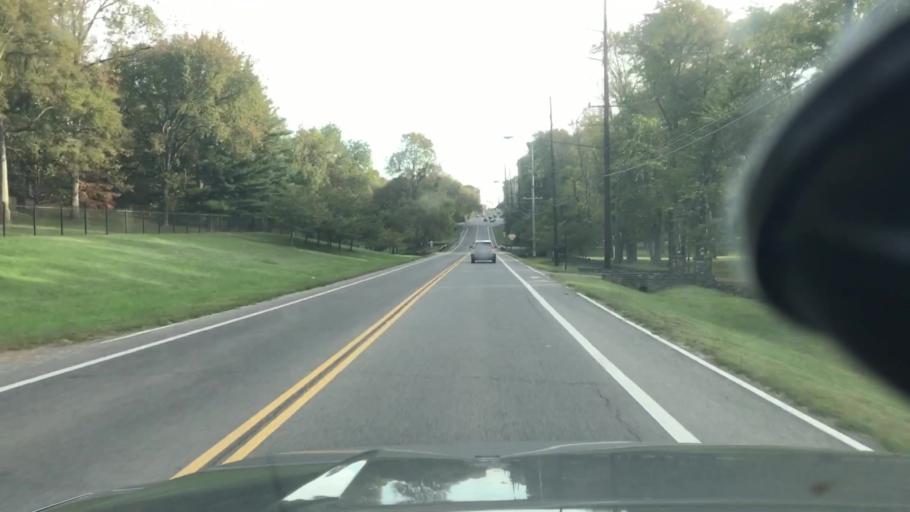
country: US
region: Tennessee
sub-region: Davidson County
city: Forest Hills
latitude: 36.0874
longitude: -86.8314
